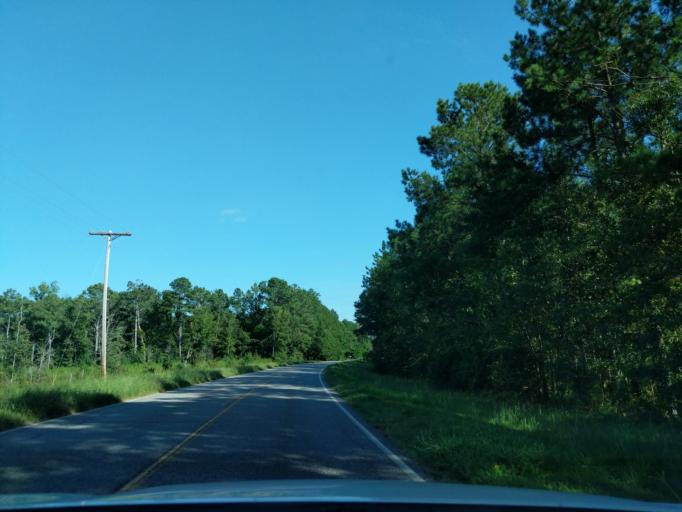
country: US
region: Georgia
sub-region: Oglethorpe County
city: Lexington
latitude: 33.9027
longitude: -82.9958
